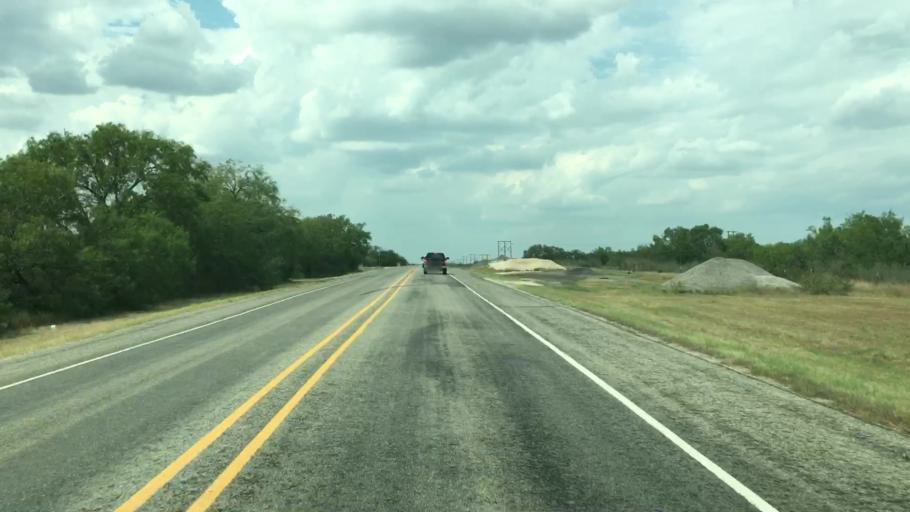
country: US
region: Texas
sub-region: Live Oak County
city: Three Rivers
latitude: 28.6452
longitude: -98.2845
